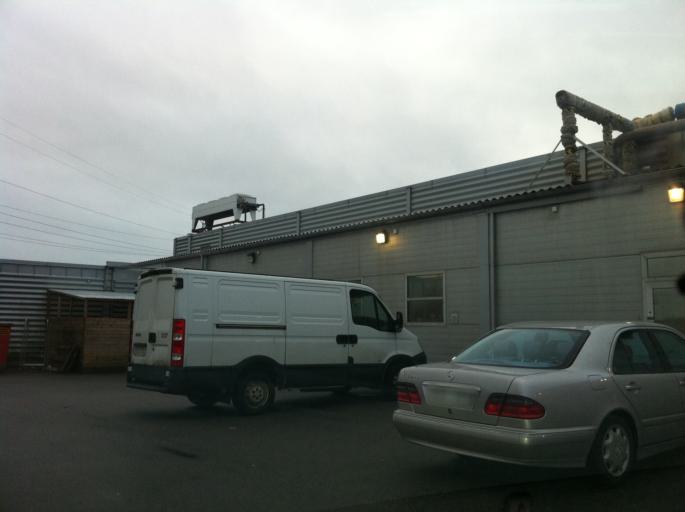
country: SE
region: Skane
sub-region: Landskrona
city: Asmundtorp
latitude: 55.8737
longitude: 12.8869
